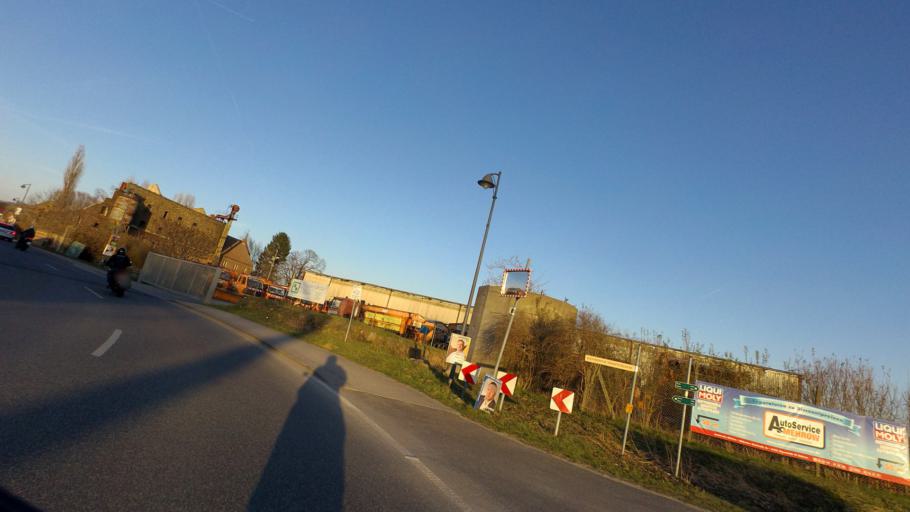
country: DE
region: Brandenburg
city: Ahrensfelde
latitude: 52.5704
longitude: 13.6139
